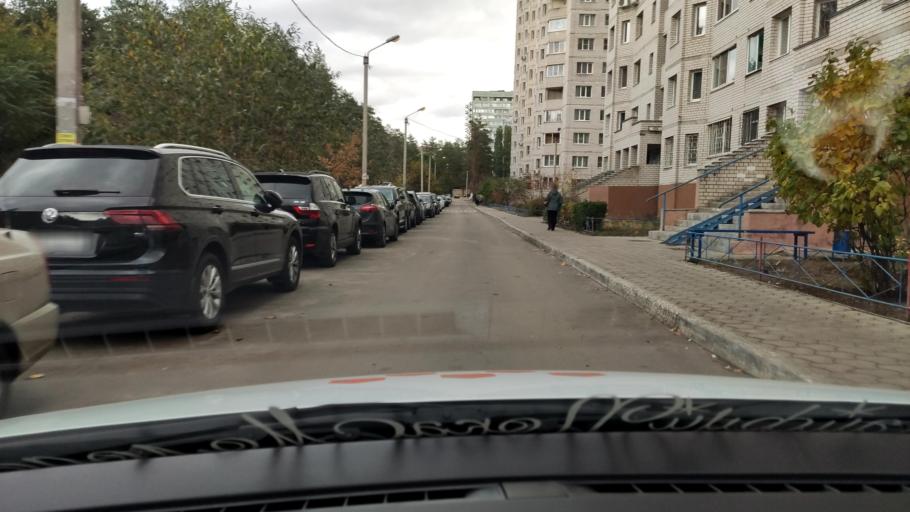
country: RU
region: Voronezj
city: Podgornoye
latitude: 51.7185
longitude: 39.1577
